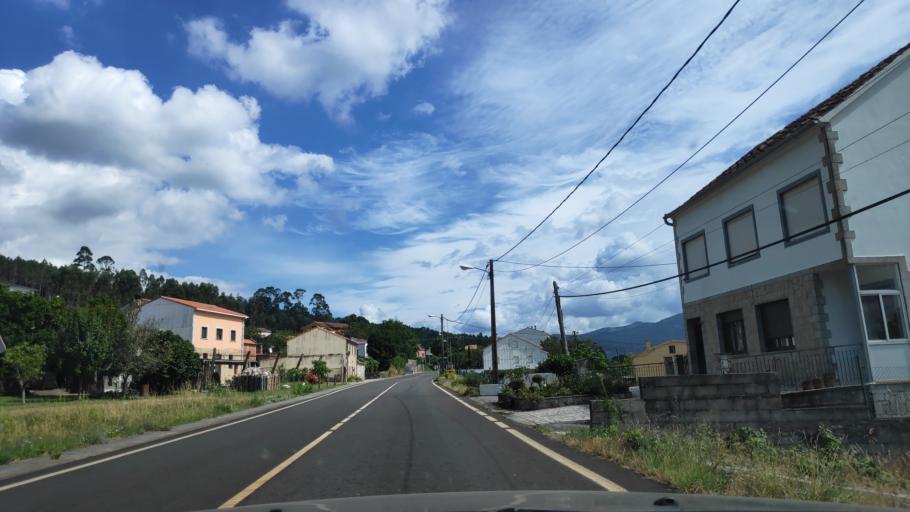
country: ES
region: Galicia
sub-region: Provincia da Coruna
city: Padron
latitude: 42.7282
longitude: -8.6738
